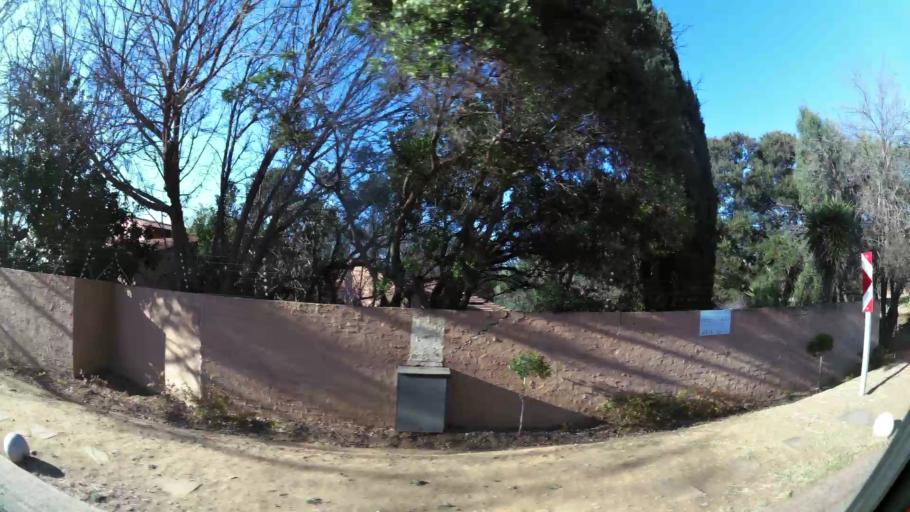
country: ZA
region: Gauteng
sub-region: City of Johannesburg Metropolitan Municipality
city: Midrand
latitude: -26.0312
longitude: 28.0494
